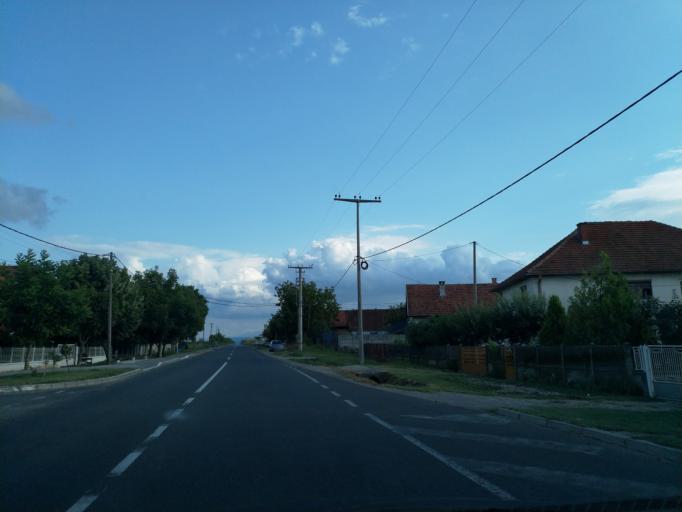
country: RS
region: Central Serbia
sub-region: Pomoravski Okrug
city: Paracin
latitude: 43.8300
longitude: 21.4170
